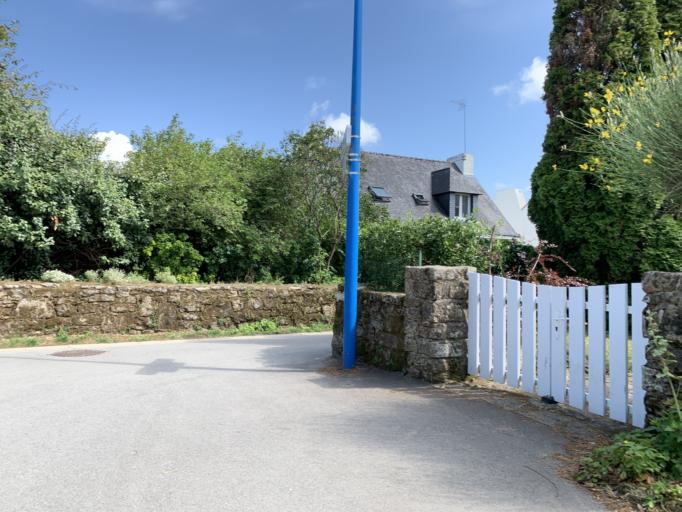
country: FR
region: Brittany
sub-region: Departement du Morbihan
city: Arradon
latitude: 47.6003
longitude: -2.8432
